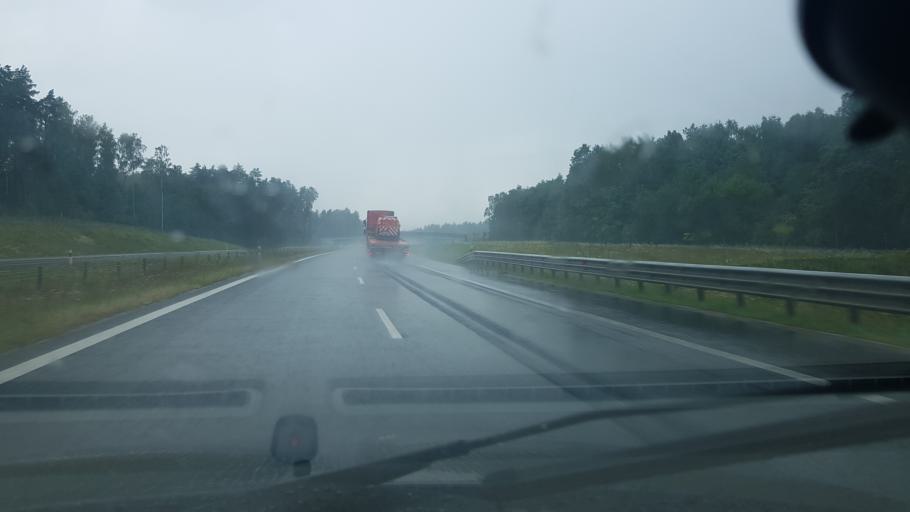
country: PL
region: Warmian-Masurian Voivodeship
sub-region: Powiat olsztynski
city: Olsztynek
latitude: 53.4565
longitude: 20.3215
